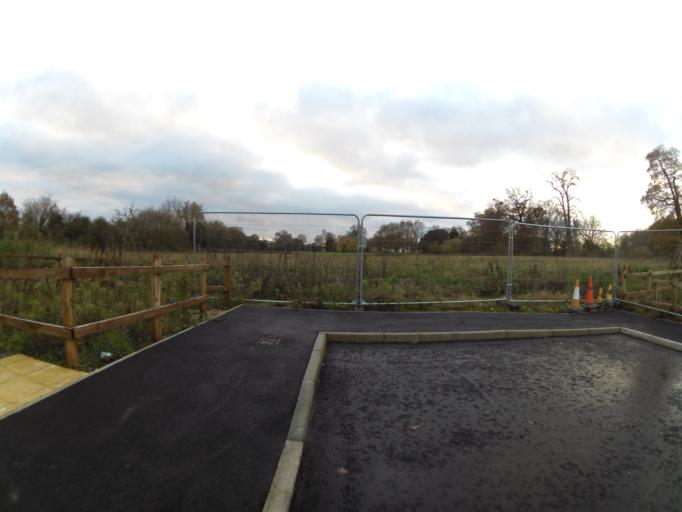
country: GB
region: England
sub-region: Suffolk
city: Bramford
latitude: 52.0586
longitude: 1.0997
